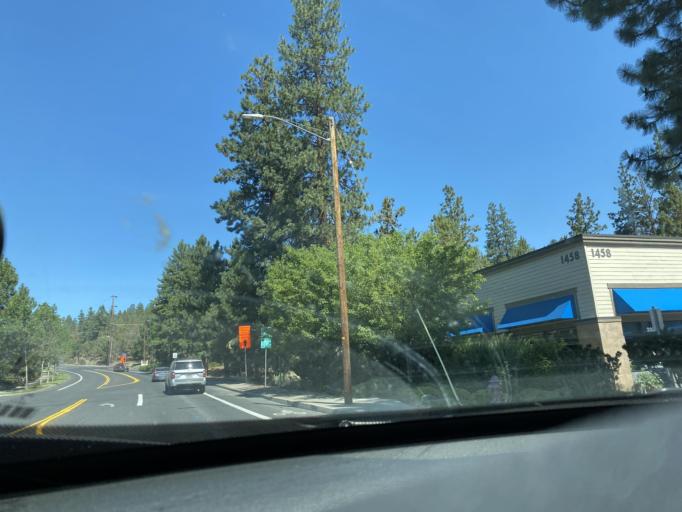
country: US
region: Oregon
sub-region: Deschutes County
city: Bend
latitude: 44.0628
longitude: -121.3381
